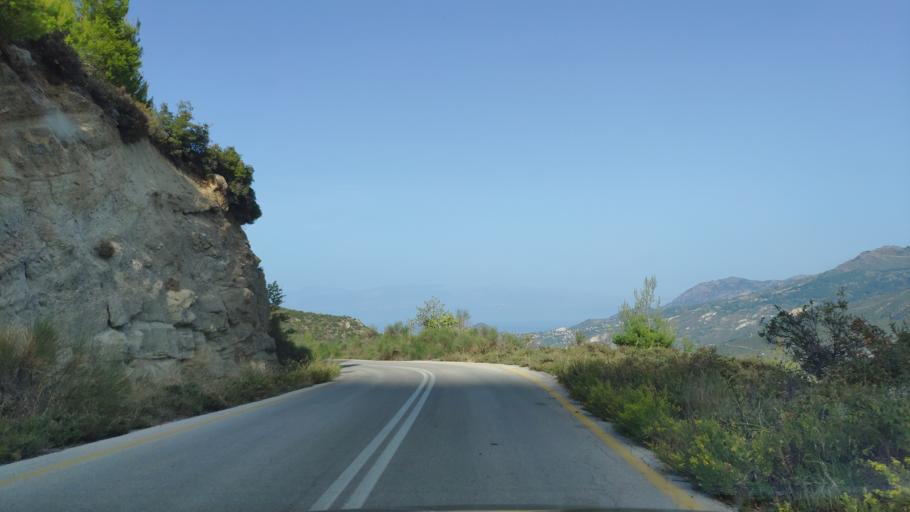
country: GR
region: West Greece
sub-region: Nomos Achaias
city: Aiyira
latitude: 38.0650
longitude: 22.3790
